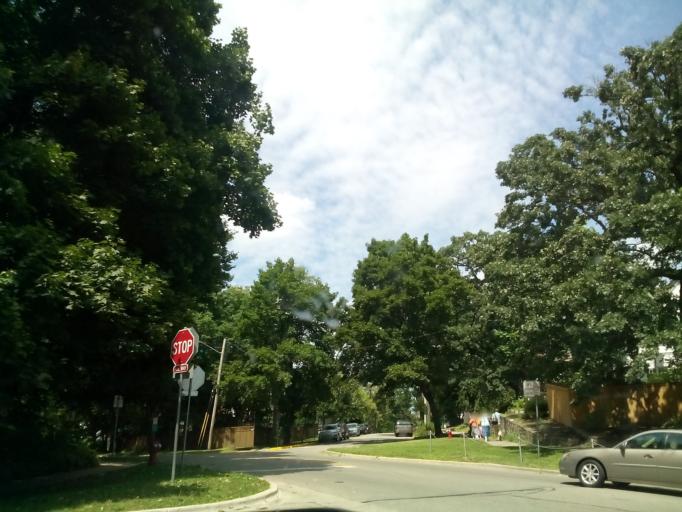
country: US
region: Wisconsin
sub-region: Dane County
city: Madison
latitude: 43.0619
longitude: -89.4122
